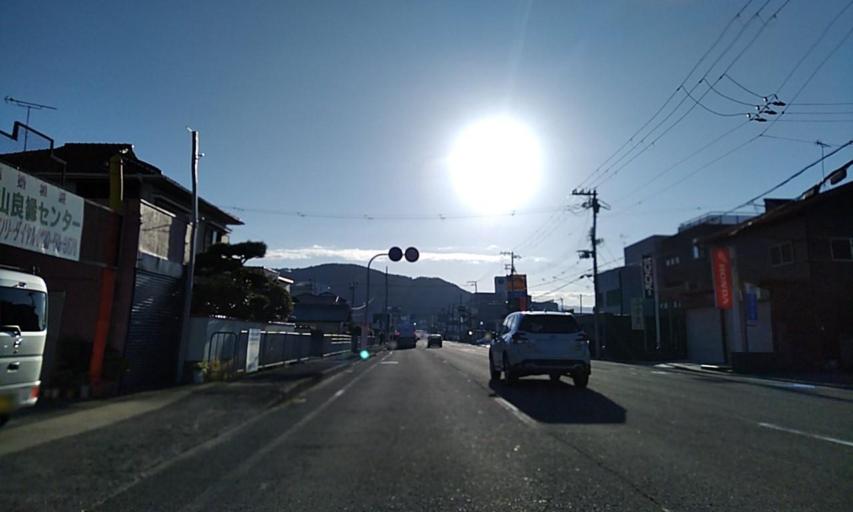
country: JP
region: Wakayama
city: Minato
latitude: 34.1896
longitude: 135.1733
